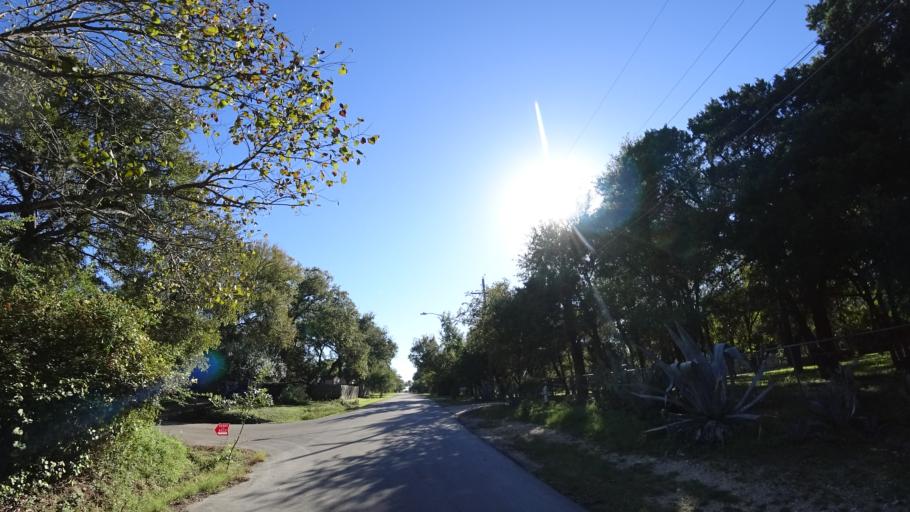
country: US
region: Texas
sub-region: Travis County
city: Rollingwood
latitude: 30.2380
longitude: -97.8085
